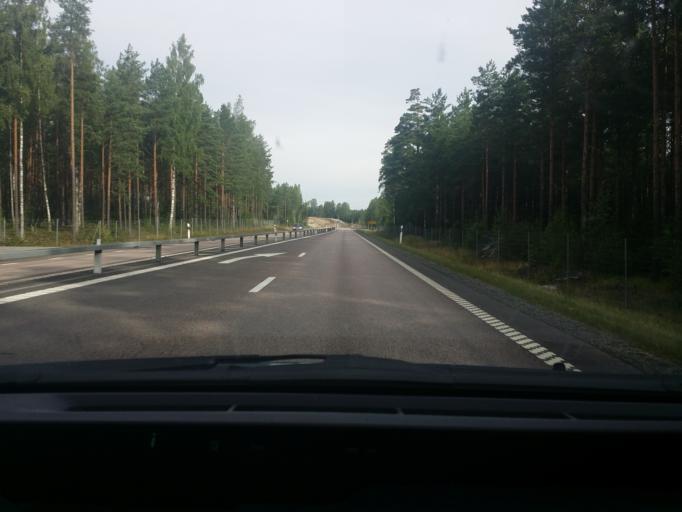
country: SE
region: Vaestmanland
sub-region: Sala Kommun
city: Sala
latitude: 59.8160
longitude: 16.5449
